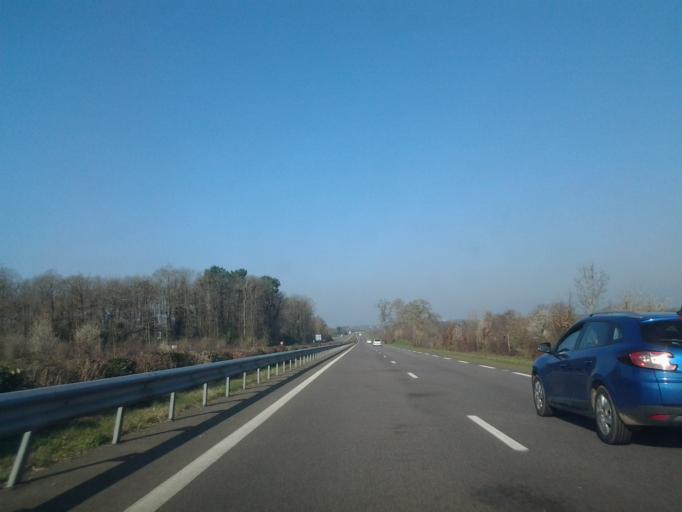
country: FR
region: Pays de la Loire
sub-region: Departement de la Vendee
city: Saint-Christophe-du-Ligneron
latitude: 46.8033
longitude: -1.7310
